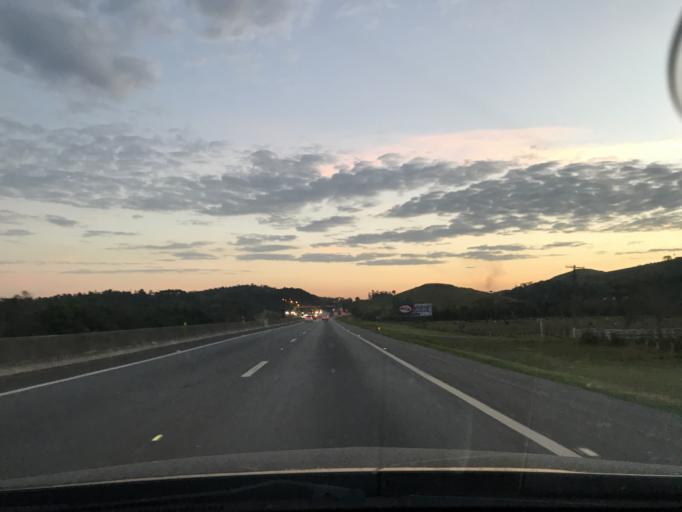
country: BR
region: Sao Paulo
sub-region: Santa Isabel
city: Santa Isabel
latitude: -23.3432
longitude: -46.1589
